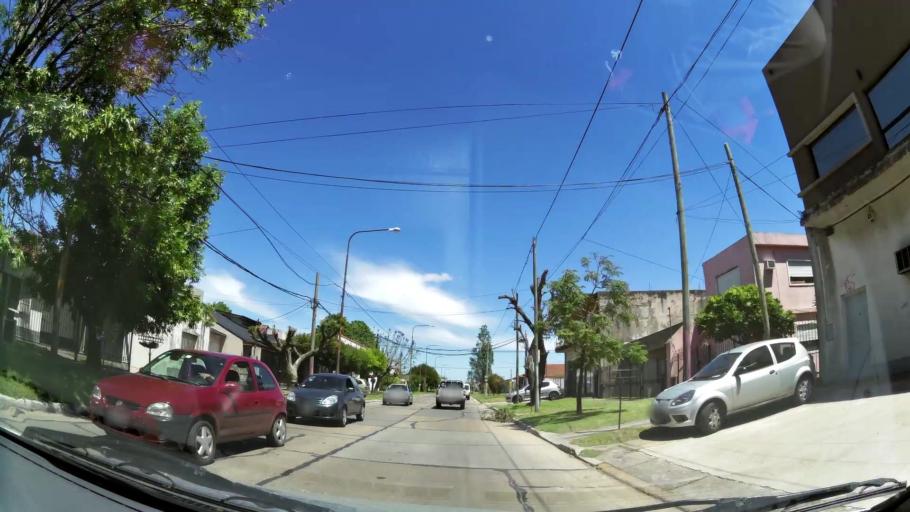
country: AR
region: Buenos Aires
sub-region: Partido de Quilmes
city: Quilmes
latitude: -34.7313
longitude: -58.2765
